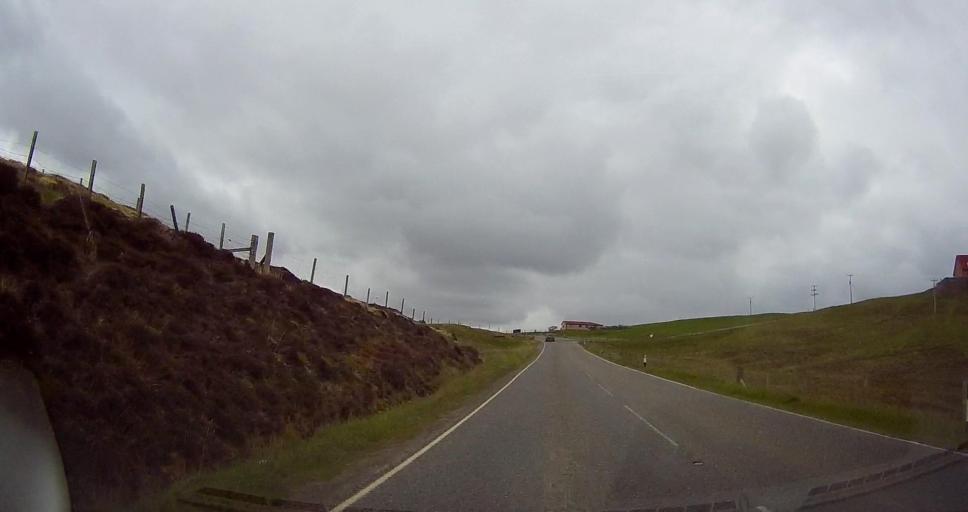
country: GB
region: Scotland
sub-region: Shetland Islands
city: Lerwick
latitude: 60.3826
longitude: -1.3425
